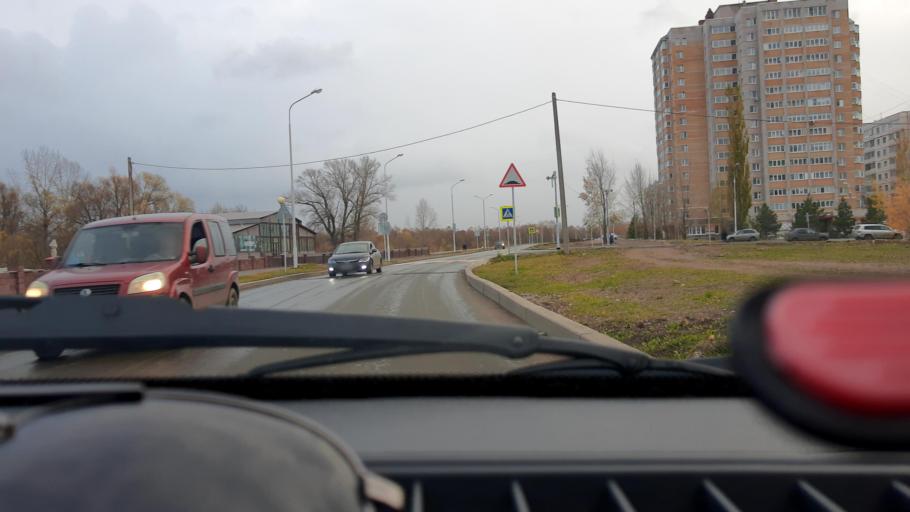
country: RU
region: Bashkortostan
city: Ufa
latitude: 54.7742
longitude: 56.0851
